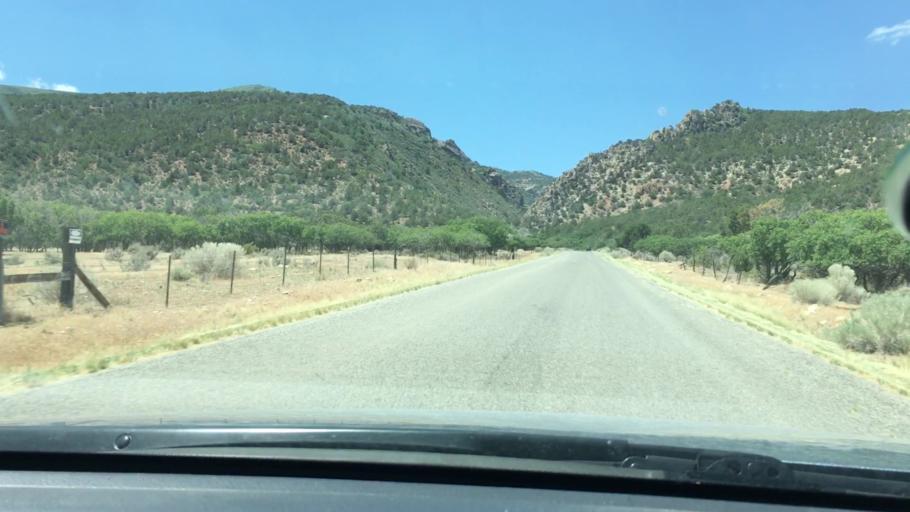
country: US
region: Utah
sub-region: Sanpete County
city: Moroni
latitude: 39.5558
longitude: -111.6543
